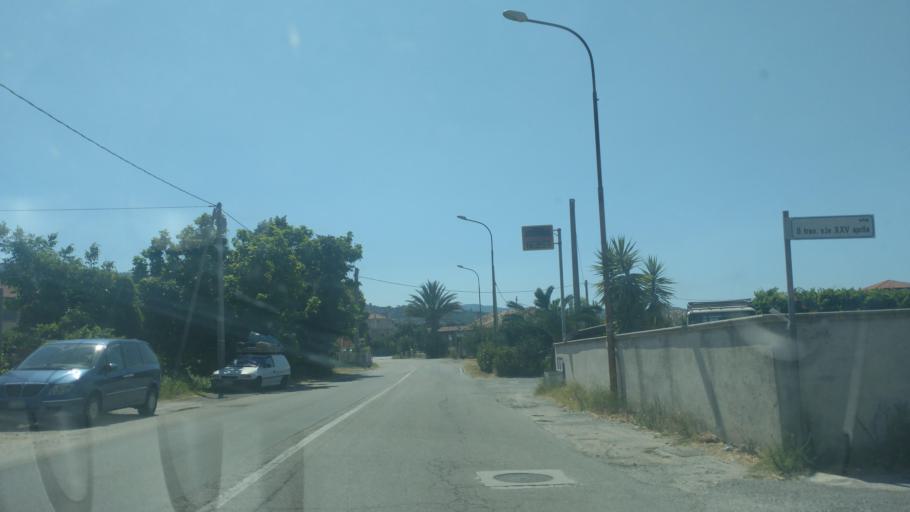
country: IT
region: Calabria
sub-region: Provincia di Catanzaro
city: Marina di Davoli
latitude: 38.6669
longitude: 16.5379
